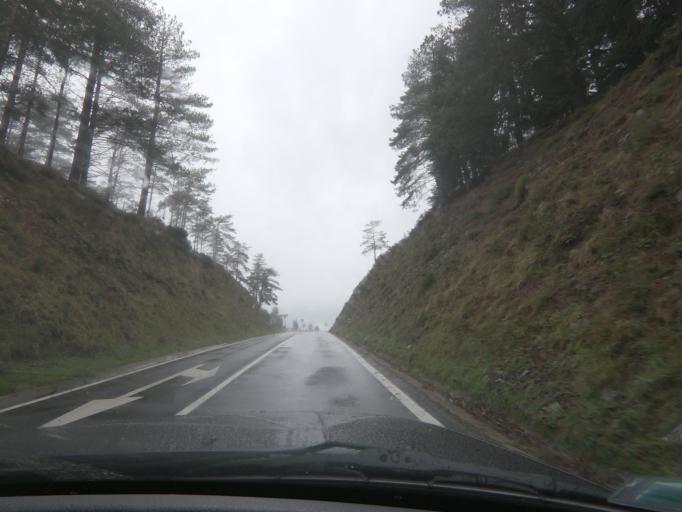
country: PT
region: Vila Real
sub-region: Mondim de Basto
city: Mondim de Basto
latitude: 41.3173
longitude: -7.8883
